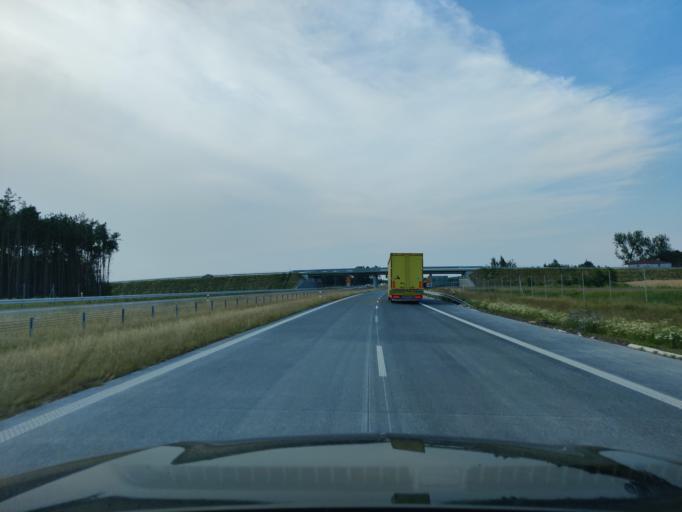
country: PL
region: Masovian Voivodeship
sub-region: Powiat mlawski
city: Strzegowo
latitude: 52.8913
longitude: 20.2633
